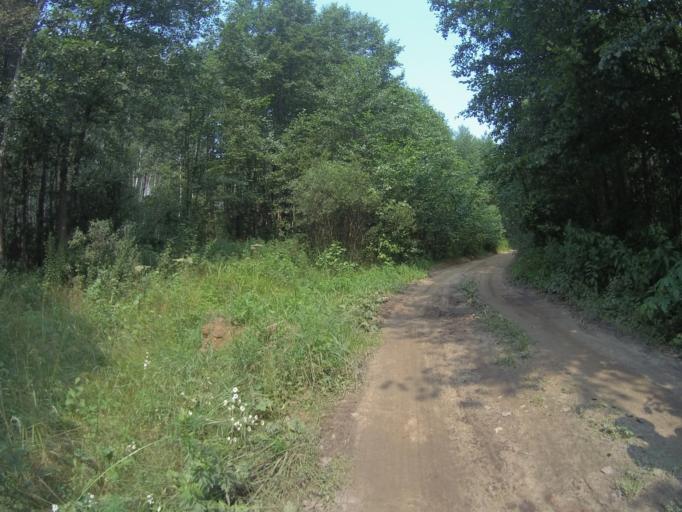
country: RU
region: Vladimir
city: Vorsha
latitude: 55.9771
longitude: 40.1870
